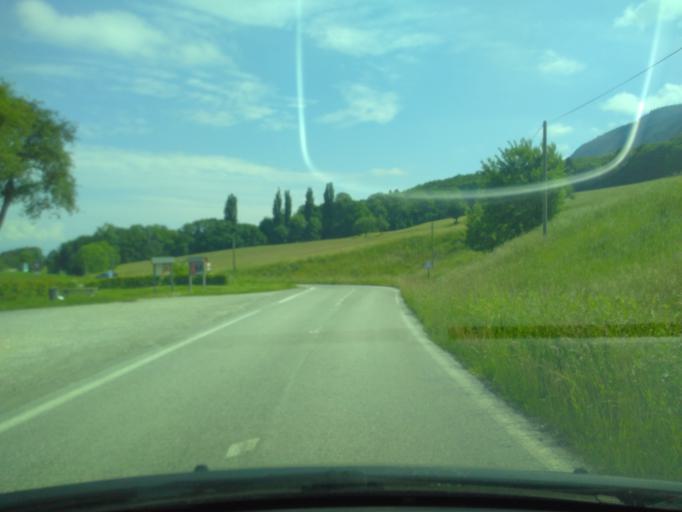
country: FR
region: Rhone-Alpes
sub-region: Departement de la Haute-Savoie
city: Beaumont
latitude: 46.0846
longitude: 6.1013
